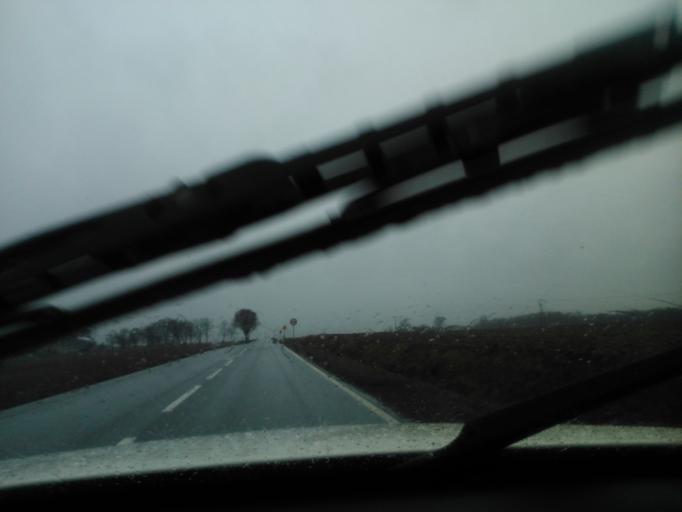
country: PL
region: Kujawsko-Pomorskie
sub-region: Powiat golubsko-dobrzynski
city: Radomin
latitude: 53.0840
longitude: 19.2179
